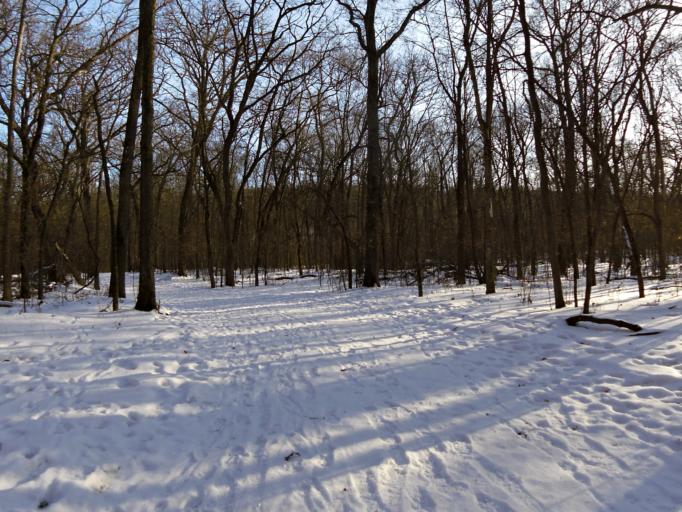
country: US
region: Wisconsin
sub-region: Saint Croix County
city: North Hudson
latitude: 45.0217
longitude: -92.6774
